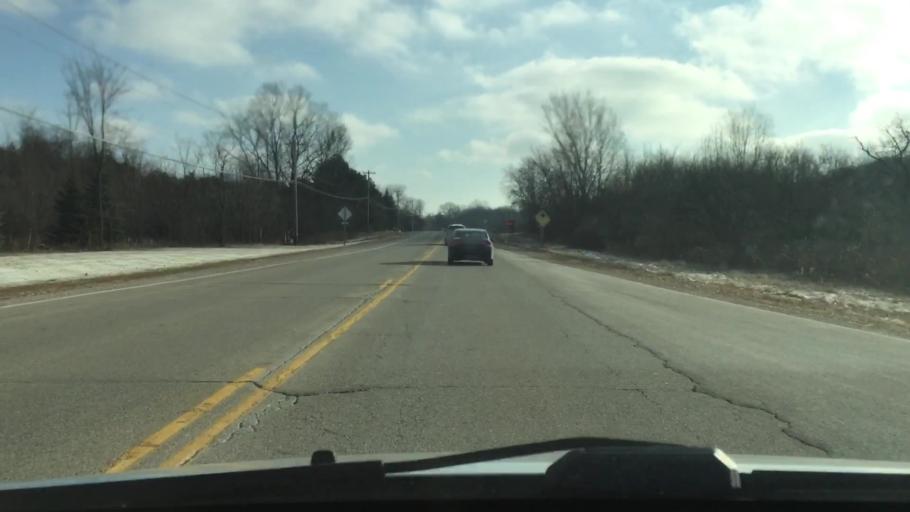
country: US
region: Wisconsin
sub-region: Waukesha County
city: Wales
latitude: 43.0124
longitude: -88.3971
